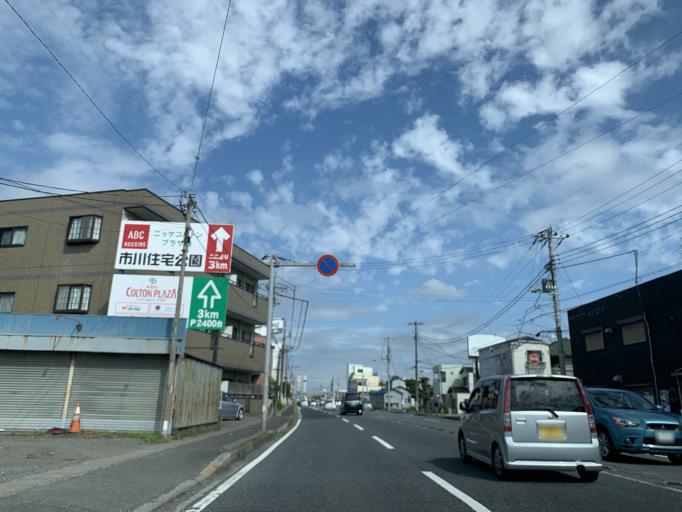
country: JP
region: Tokyo
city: Urayasu
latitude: 35.6946
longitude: 139.9233
